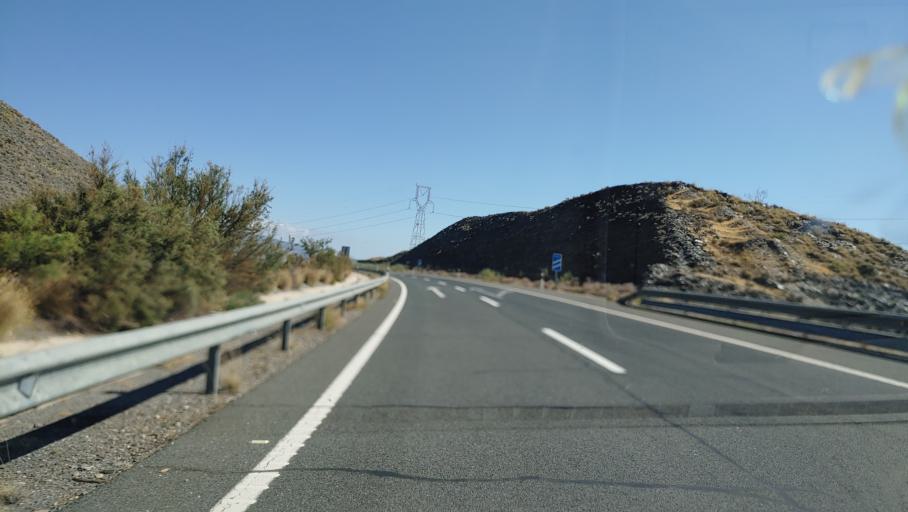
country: ES
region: Andalusia
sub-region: Provincia de Almeria
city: Gergal
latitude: 37.0972
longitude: -2.5289
